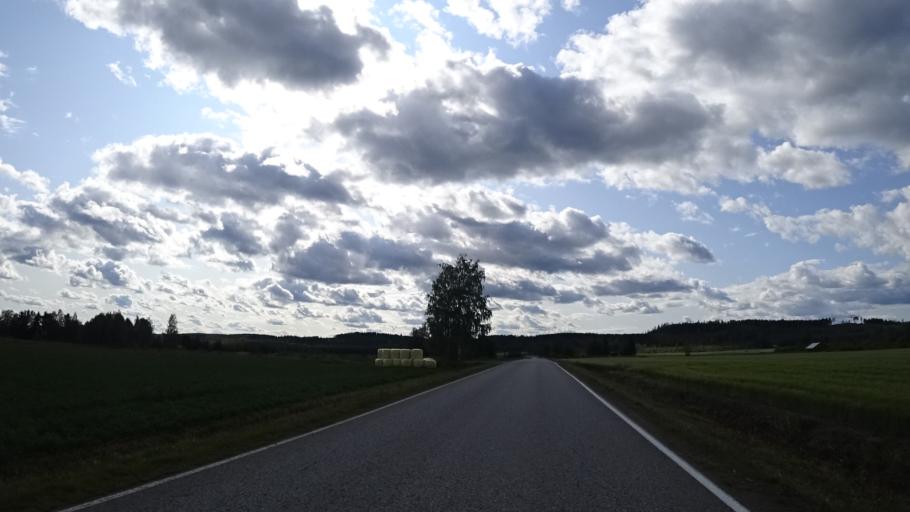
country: RU
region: Republic of Karelia
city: Vyartsilya
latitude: 62.2215
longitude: 30.6277
